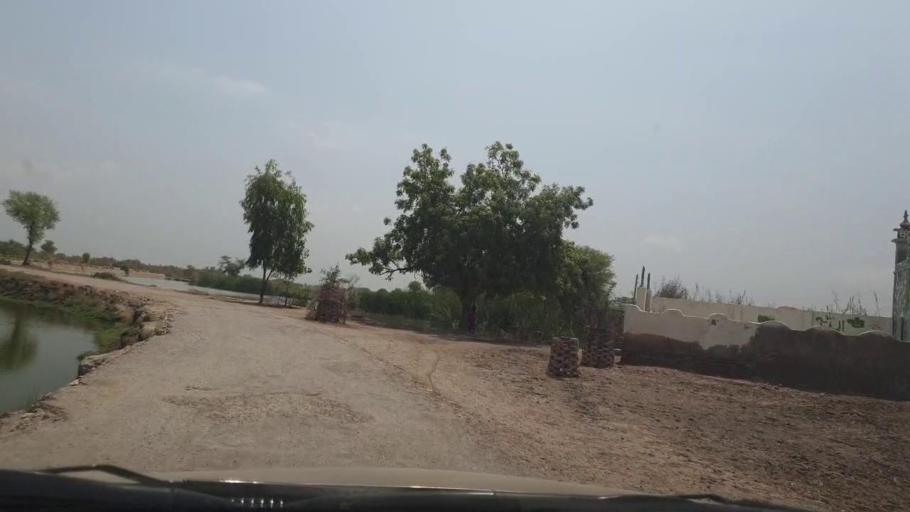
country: PK
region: Sindh
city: Ratodero
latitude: 27.7338
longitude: 68.3069
